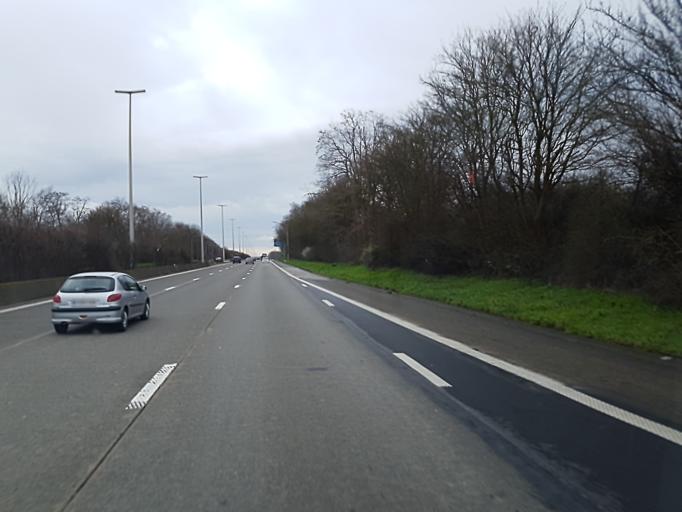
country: BE
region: Flanders
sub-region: Provincie Vlaams-Brabant
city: Tienen
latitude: 50.7482
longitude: 4.9571
